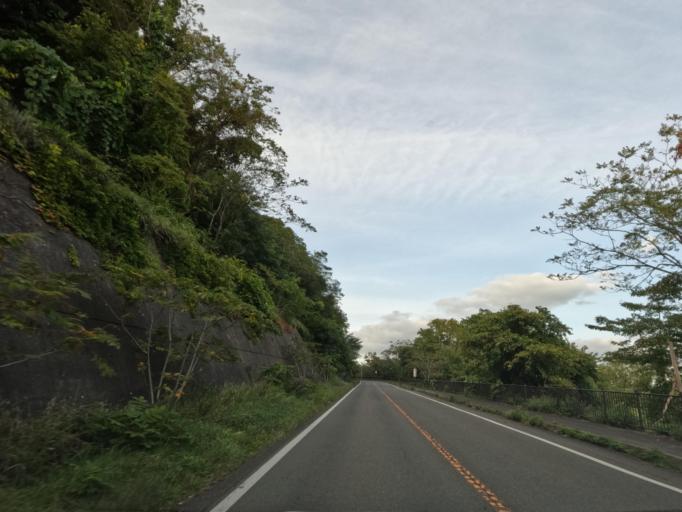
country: JP
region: Hokkaido
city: Date
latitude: 42.5237
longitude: 140.8617
